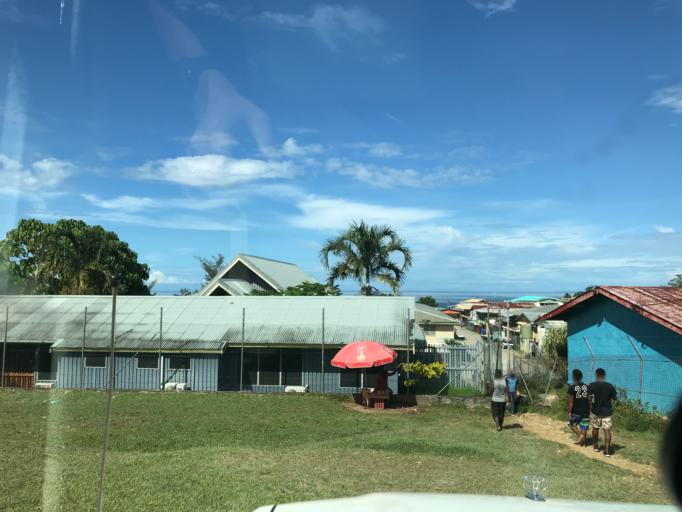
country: SB
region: Malaita
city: Auki
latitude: -8.7713
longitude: 160.6988
